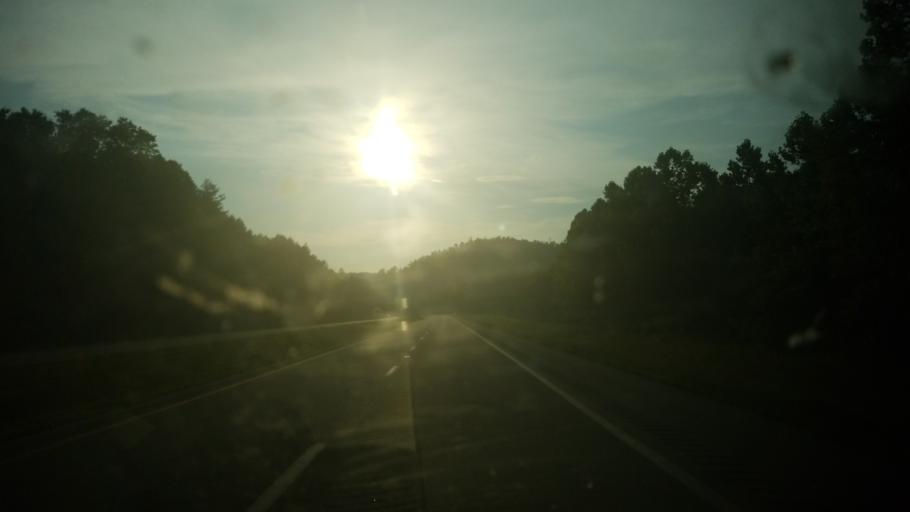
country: US
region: Ohio
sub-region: Pike County
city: Piketon
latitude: 39.0501
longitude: -83.1882
